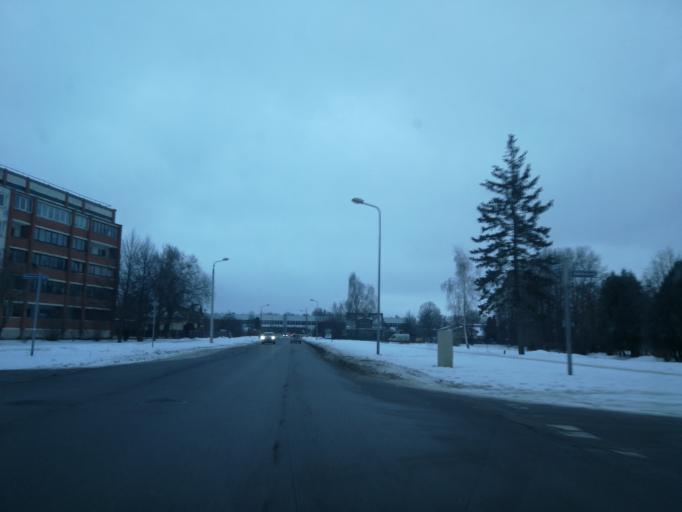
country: LV
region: Riga
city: Riga
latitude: 56.9430
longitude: 24.1742
